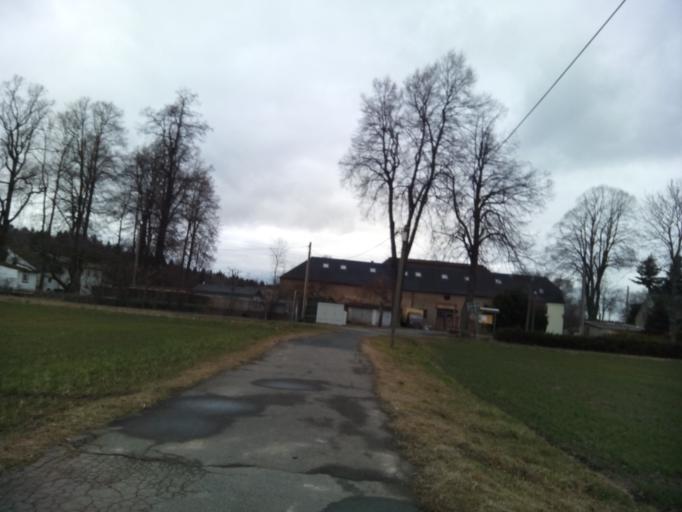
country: DE
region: Saxony
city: Freiberg
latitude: 50.8909
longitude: 13.3321
